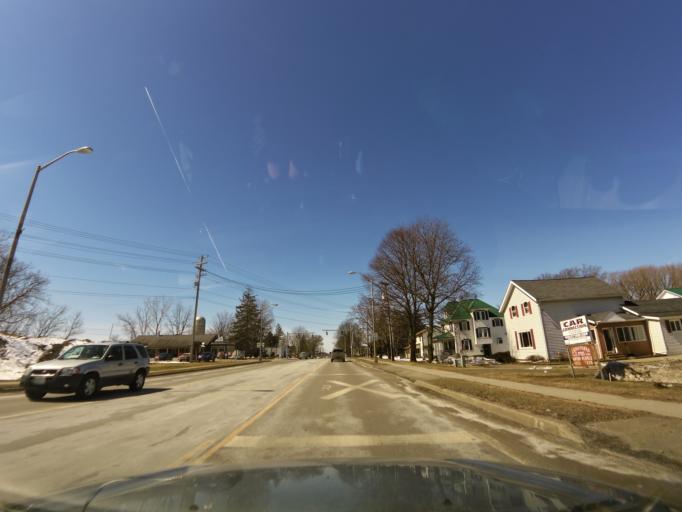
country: US
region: New York
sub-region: Wyoming County
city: Arcade
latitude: 42.5338
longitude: -78.4328
